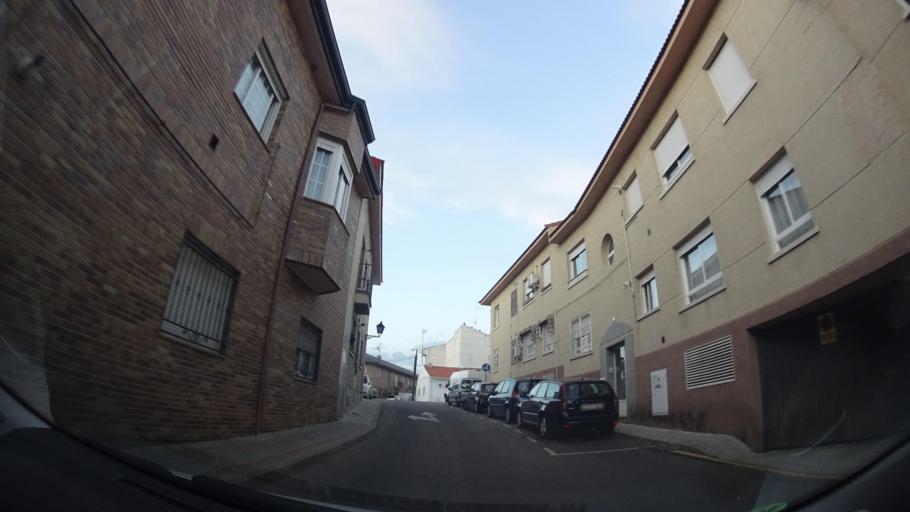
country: ES
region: Madrid
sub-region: Provincia de Madrid
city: Colmenarejo
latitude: 40.5619
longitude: -4.0178
